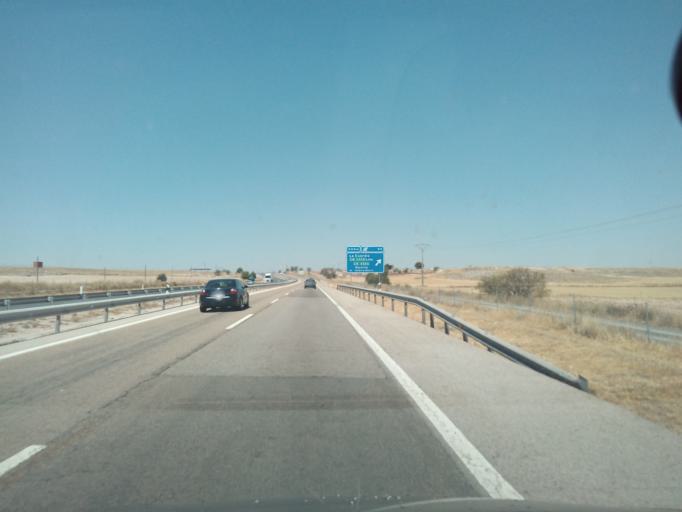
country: ES
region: Castille-La Mancha
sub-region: Province of Toledo
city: Tembleque
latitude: 39.7575
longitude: -3.4825
